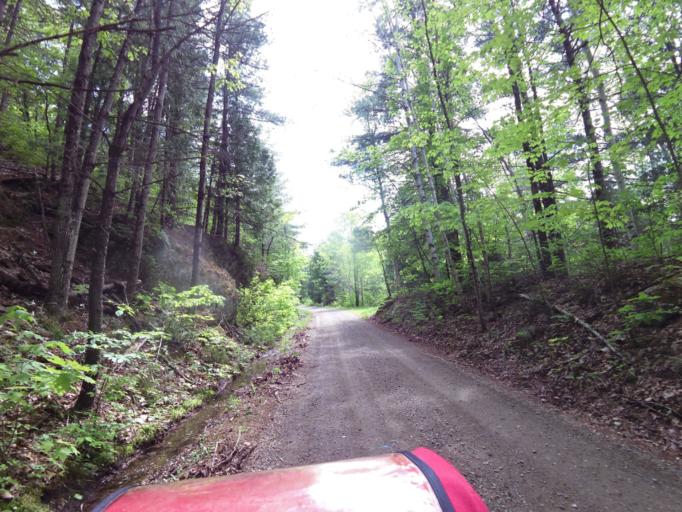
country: CA
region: Ontario
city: Renfrew
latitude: 45.1933
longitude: -76.6863
